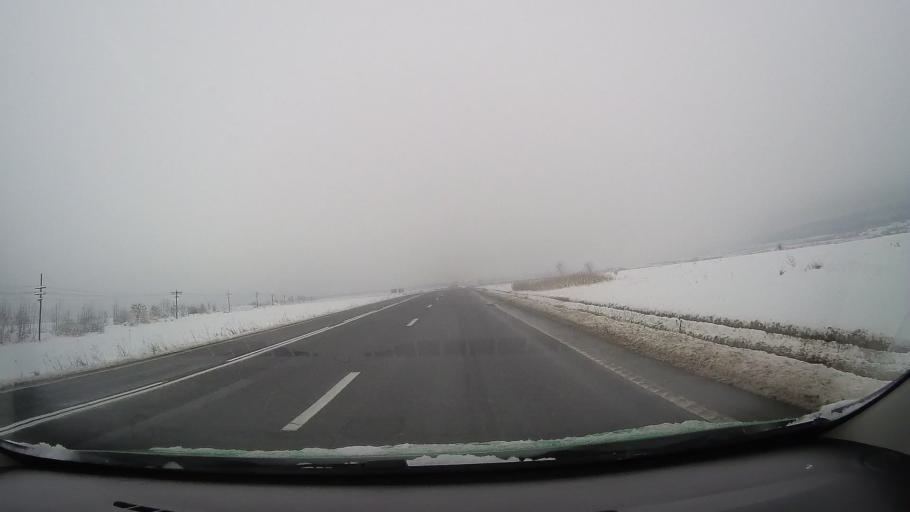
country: RO
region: Sibiu
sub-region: Oras Saliste
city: Saliste
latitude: 45.7931
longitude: 23.9171
